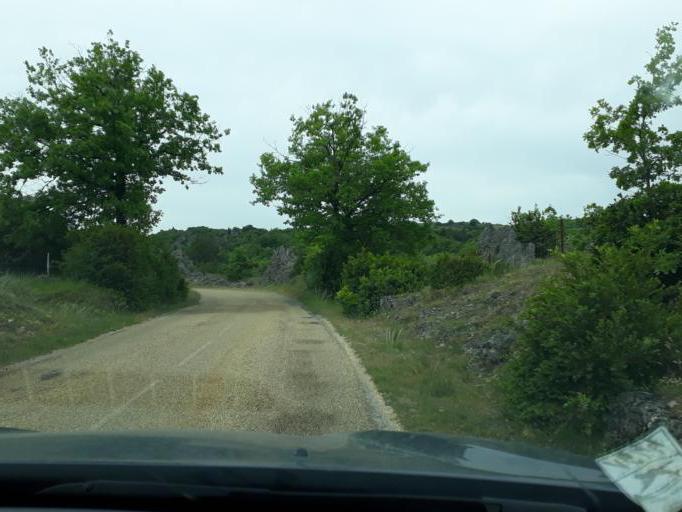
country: FR
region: Languedoc-Roussillon
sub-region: Departement de l'Herault
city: Lodeve
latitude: 43.8527
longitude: 3.2671
